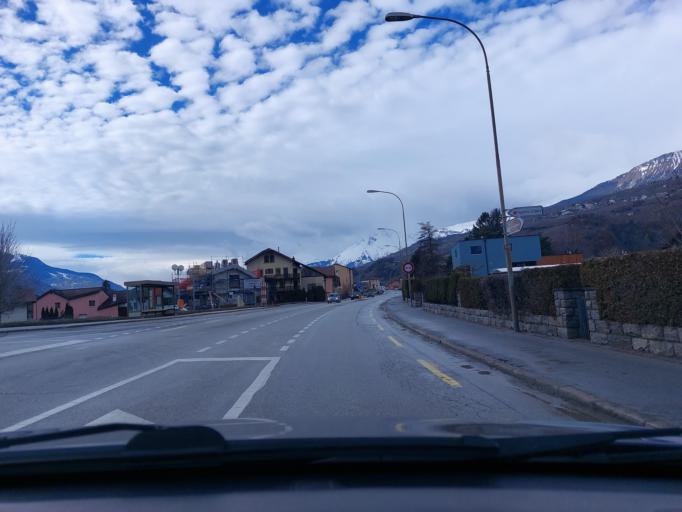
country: CH
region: Valais
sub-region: Sion District
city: Saint-Leonard
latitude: 46.2537
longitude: 7.4225
